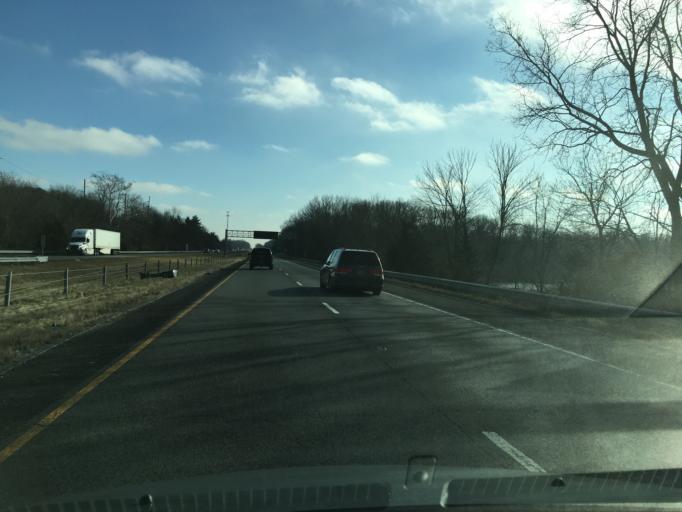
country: US
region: Indiana
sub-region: Boone County
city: Zionsville
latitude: 39.8871
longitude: -86.3011
